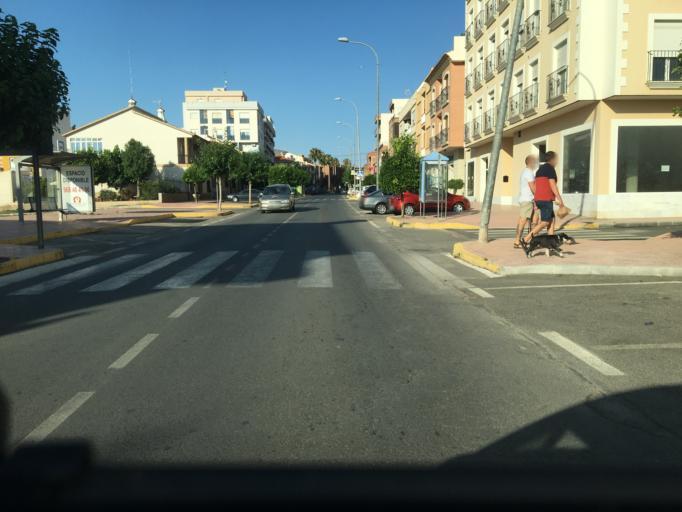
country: ES
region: Murcia
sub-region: Murcia
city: Puerto Lumbreras
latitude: 37.5652
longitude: -1.8030
